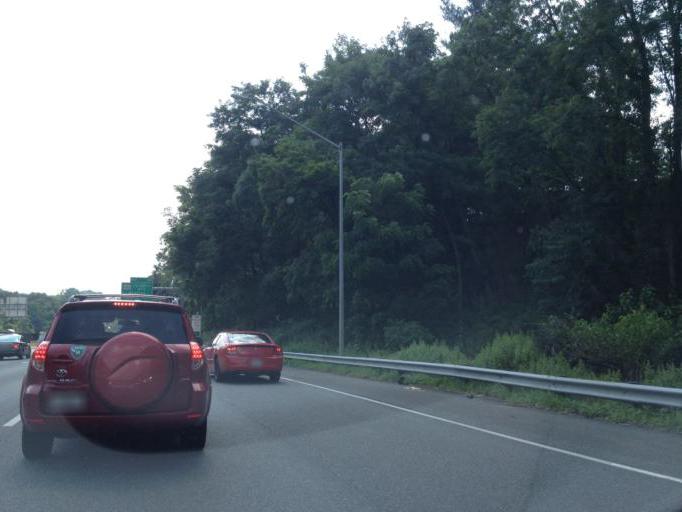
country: US
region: Maryland
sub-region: Montgomery County
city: Hillandale
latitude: 39.0187
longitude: -76.9904
